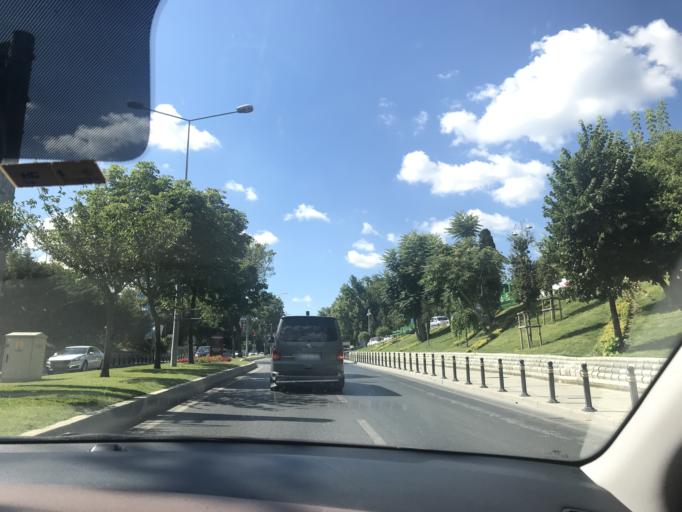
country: TR
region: Istanbul
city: UEskuedar
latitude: 41.0083
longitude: 29.0236
